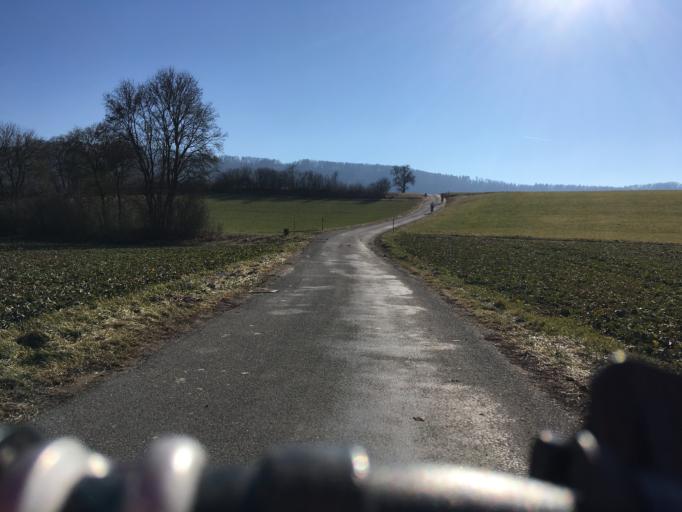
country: DE
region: Baden-Wuerttemberg
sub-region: Freiburg Region
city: Gottmadingen
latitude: 47.7195
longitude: 8.7701
